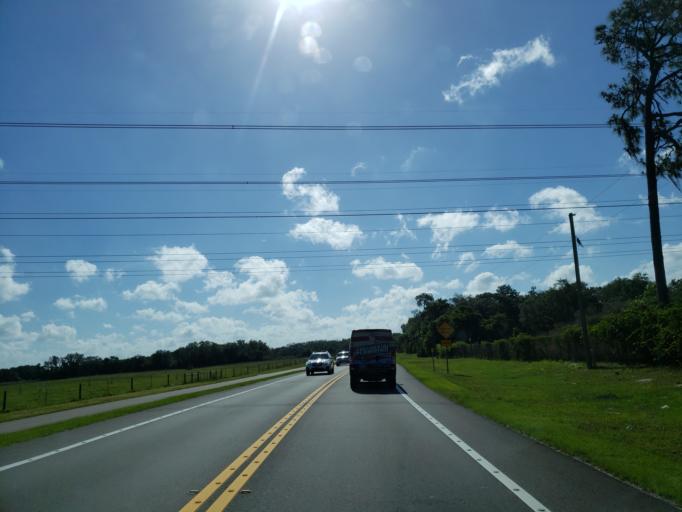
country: US
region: Florida
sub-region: Hillsborough County
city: Keystone
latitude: 28.1455
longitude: -82.6542
